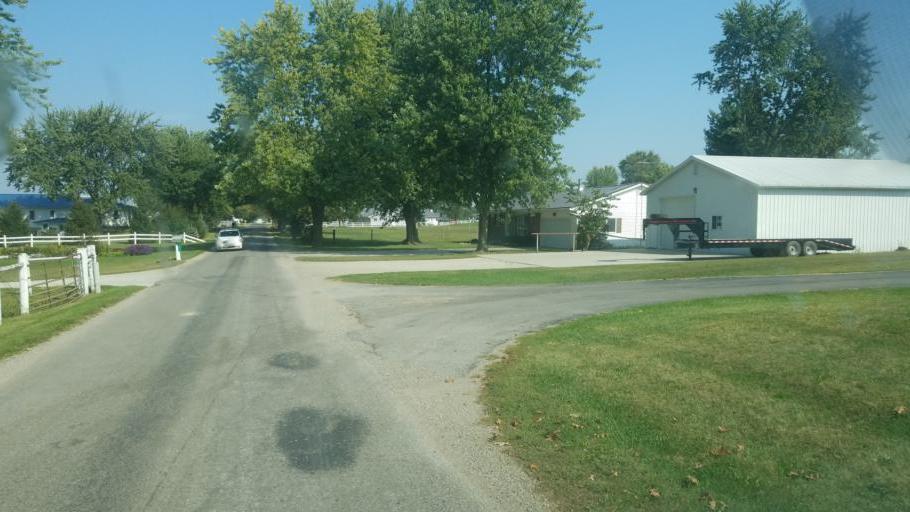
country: US
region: Indiana
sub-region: LaGrange County
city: Topeka
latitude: 41.6701
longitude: -85.5611
